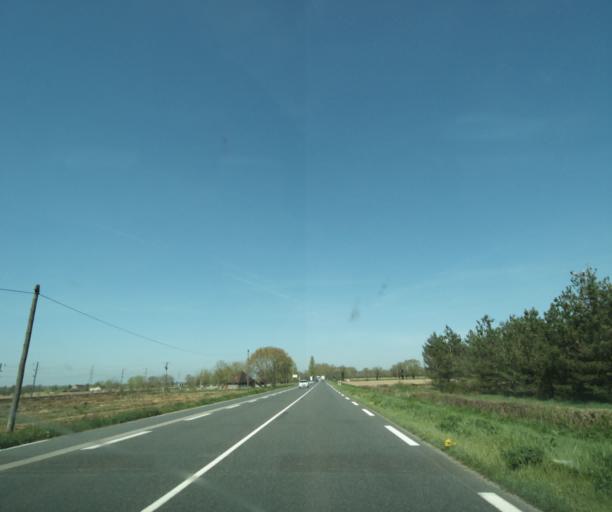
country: FR
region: Bourgogne
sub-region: Departement de la Nievre
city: Chantenay-Saint-Imbert
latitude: 46.6822
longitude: 3.2256
